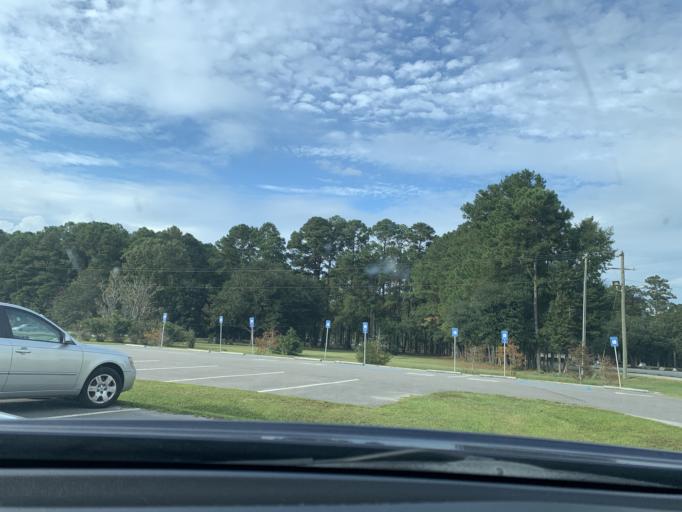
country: US
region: Georgia
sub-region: Chatham County
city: Pooler
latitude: 32.1068
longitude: -81.2511
